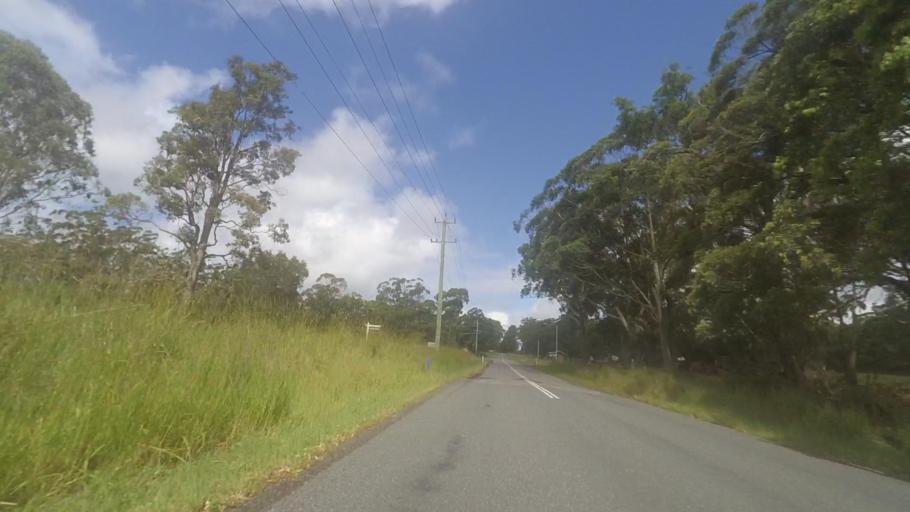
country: AU
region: New South Wales
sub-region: Great Lakes
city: Bulahdelah
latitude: -32.3879
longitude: 152.4162
